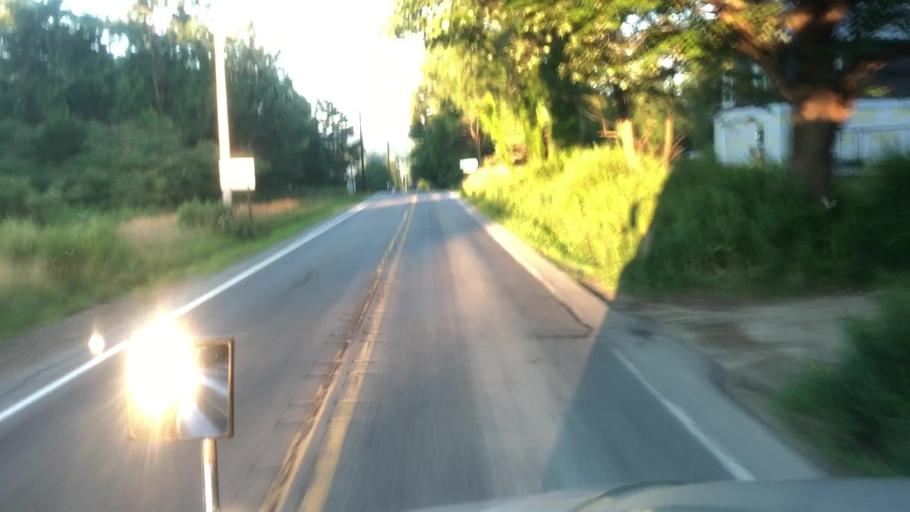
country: US
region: Pennsylvania
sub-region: Venango County
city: Hasson Heights
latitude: 41.5005
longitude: -79.6400
